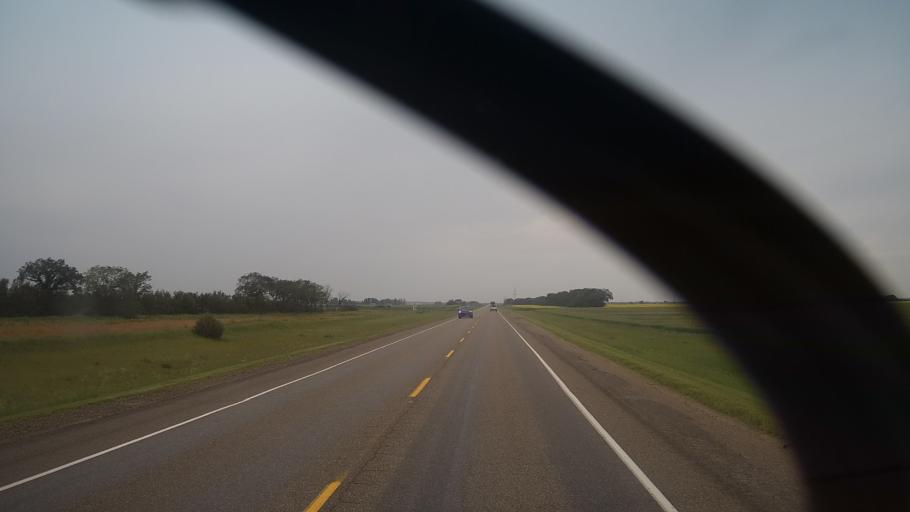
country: CA
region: Saskatchewan
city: Saskatoon
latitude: 52.1292
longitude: -106.8309
